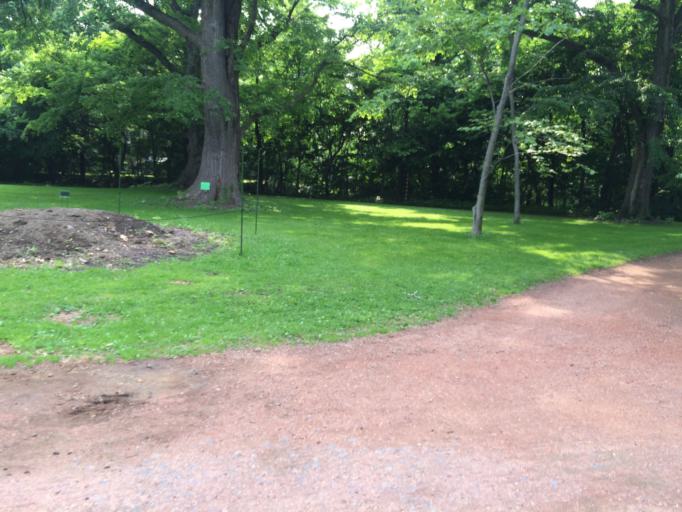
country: JP
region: Hokkaido
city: Sapporo
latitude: 43.0638
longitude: 141.3442
